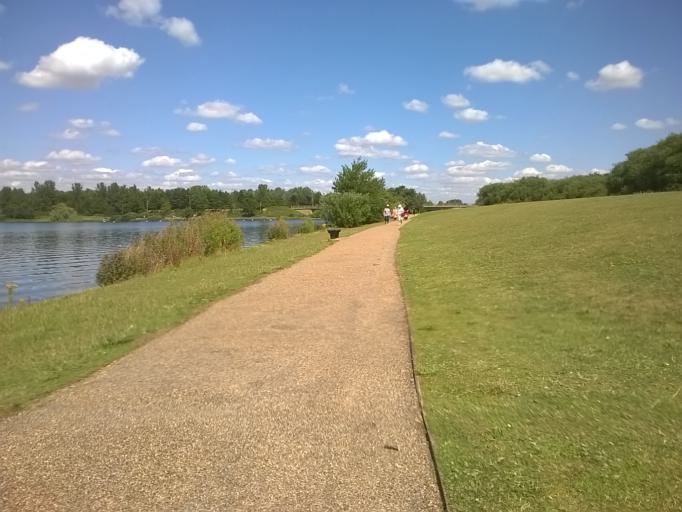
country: GB
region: England
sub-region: Milton Keynes
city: Broughton
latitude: 52.0522
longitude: -0.7151
